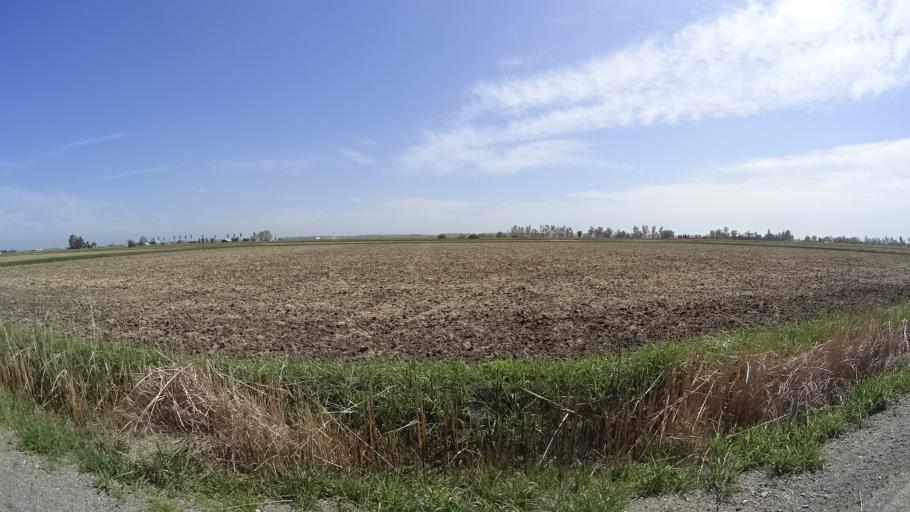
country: US
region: California
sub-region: Glenn County
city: Hamilton City
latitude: 39.5882
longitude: -122.0465
